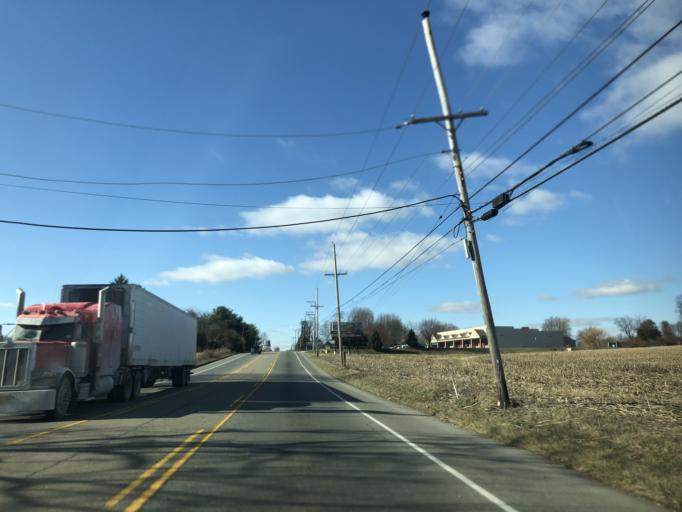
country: US
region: Pennsylvania
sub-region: Chester County
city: Parkesburg
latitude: 39.9852
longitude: -75.9482
